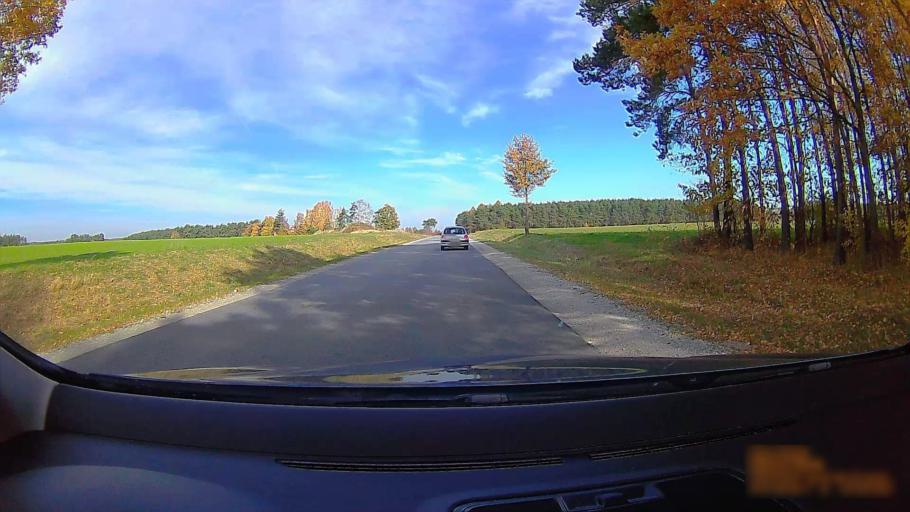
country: PL
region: Greater Poland Voivodeship
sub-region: Powiat ostrzeszowski
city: Doruchow
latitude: 51.3713
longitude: 18.0351
